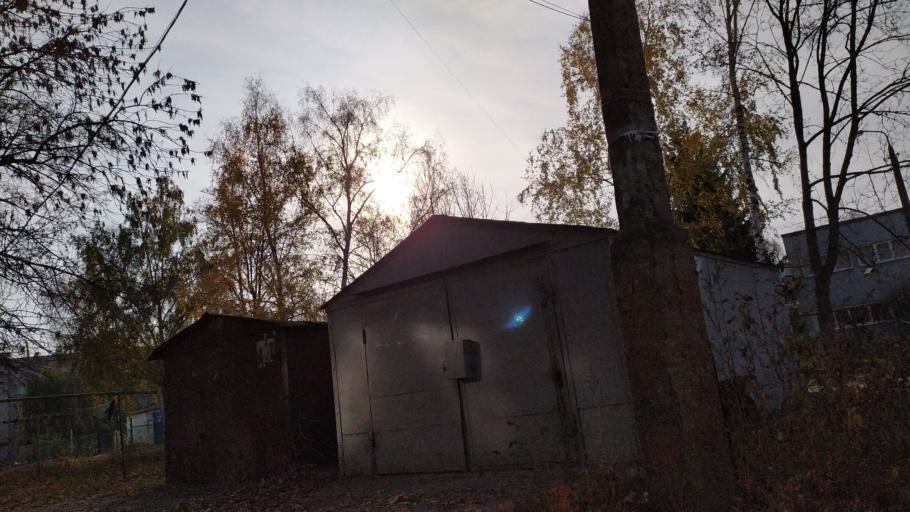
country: RU
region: Kursk
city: Kursk
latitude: 51.6482
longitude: 36.1390
